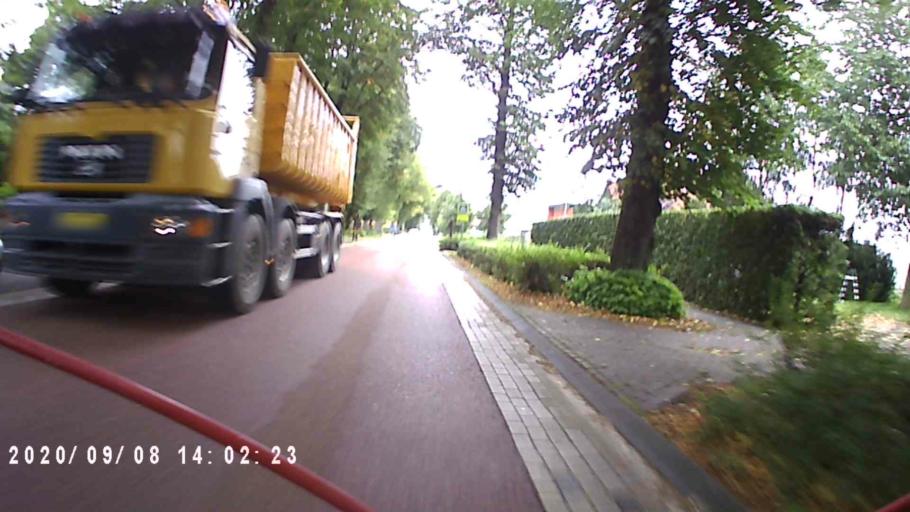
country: NL
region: Groningen
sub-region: Gemeente Veendam
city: Veendam
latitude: 53.1645
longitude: 6.8625
